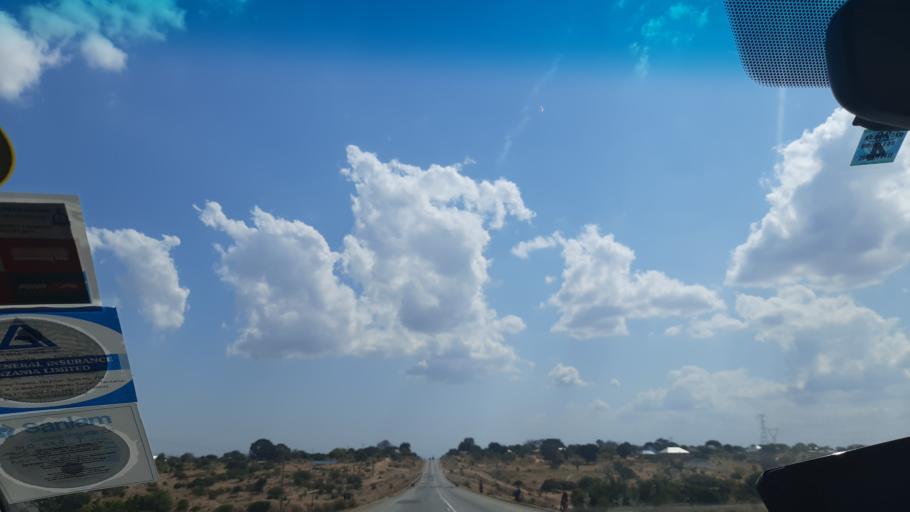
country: TZ
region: Singida
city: Kintinku
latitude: -6.0156
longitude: 35.4408
